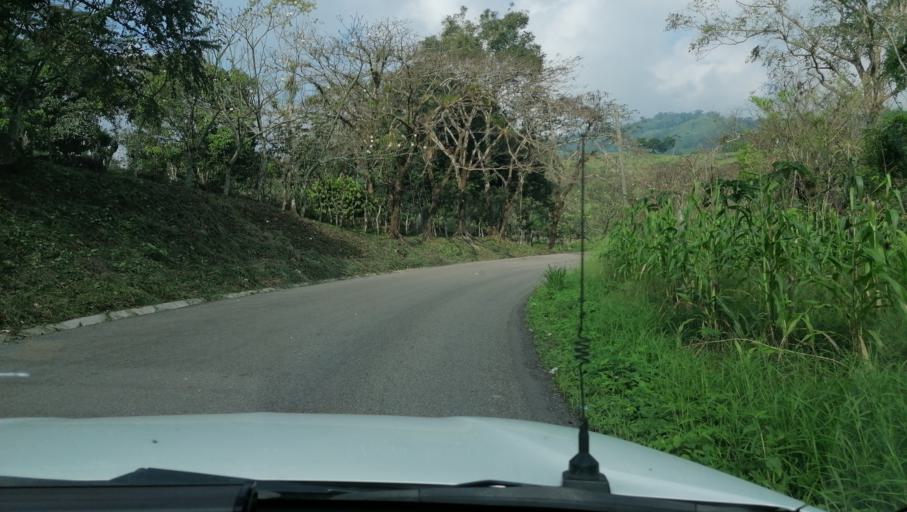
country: MX
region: Chiapas
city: Pichucalco
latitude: 17.5301
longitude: -93.1560
